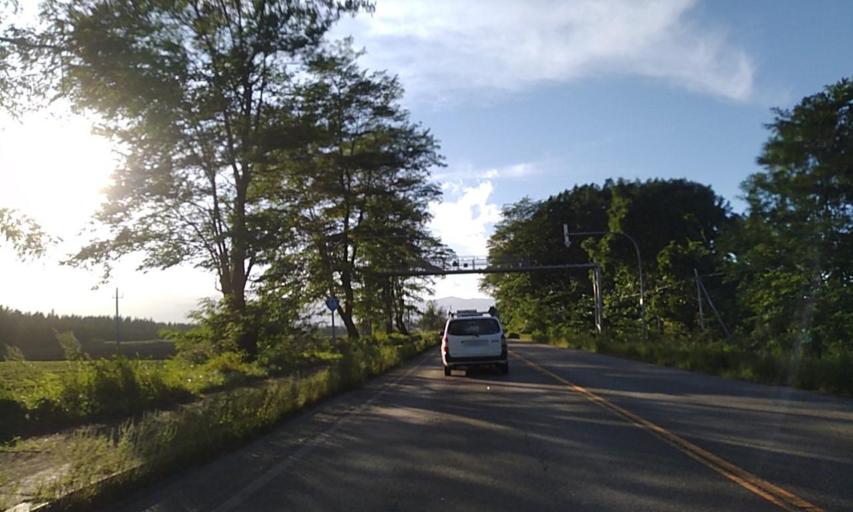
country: JP
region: Hokkaido
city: Obihiro
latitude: 42.9347
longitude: 142.9690
